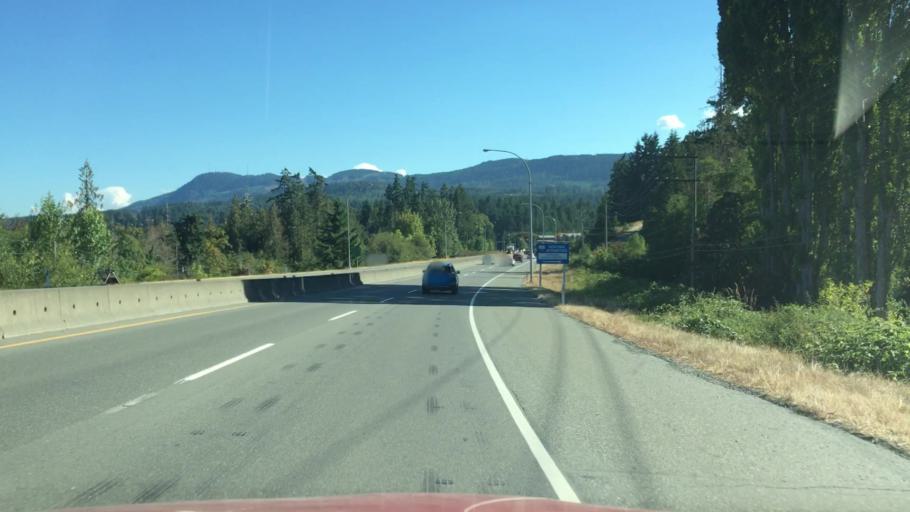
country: CA
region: British Columbia
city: North Saanich
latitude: 48.6620
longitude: -123.5597
